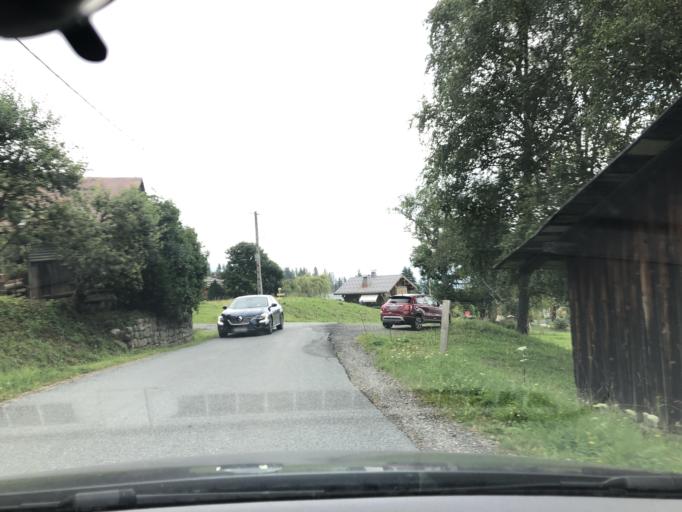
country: FR
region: Rhone-Alpes
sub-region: Departement de la Haute-Savoie
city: Combloux
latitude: 45.8980
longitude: 6.6188
